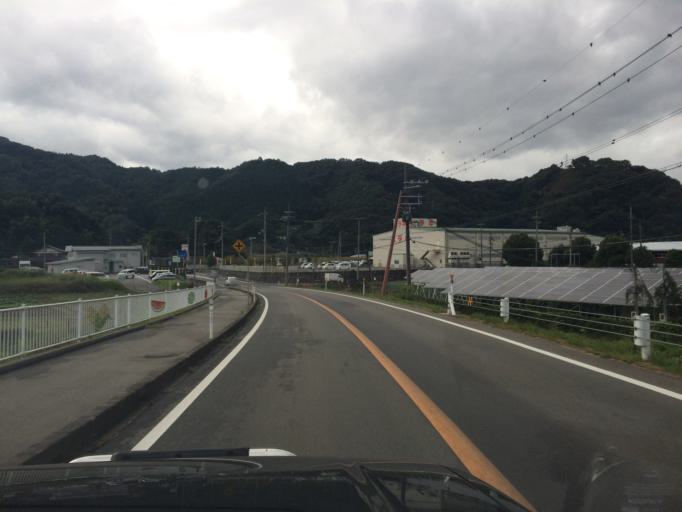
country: JP
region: Hyogo
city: Toyooka
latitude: 35.4555
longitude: 134.7751
